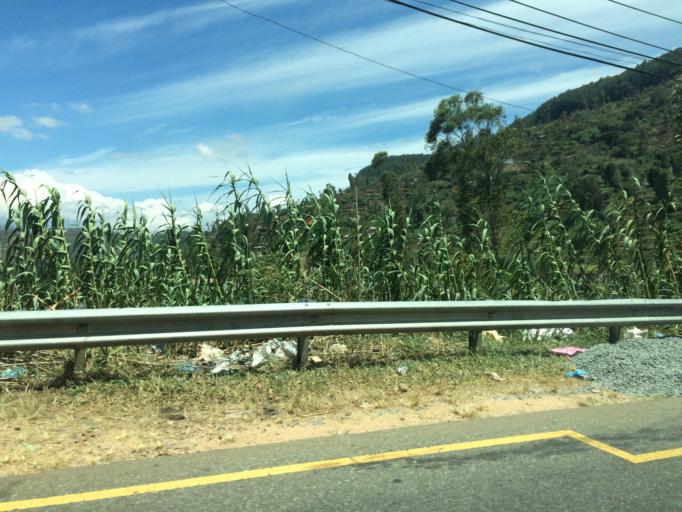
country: LK
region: Central
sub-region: Nuwara Eliya District
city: Nuwara Eliya
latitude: 6.9094
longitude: 80.8381
